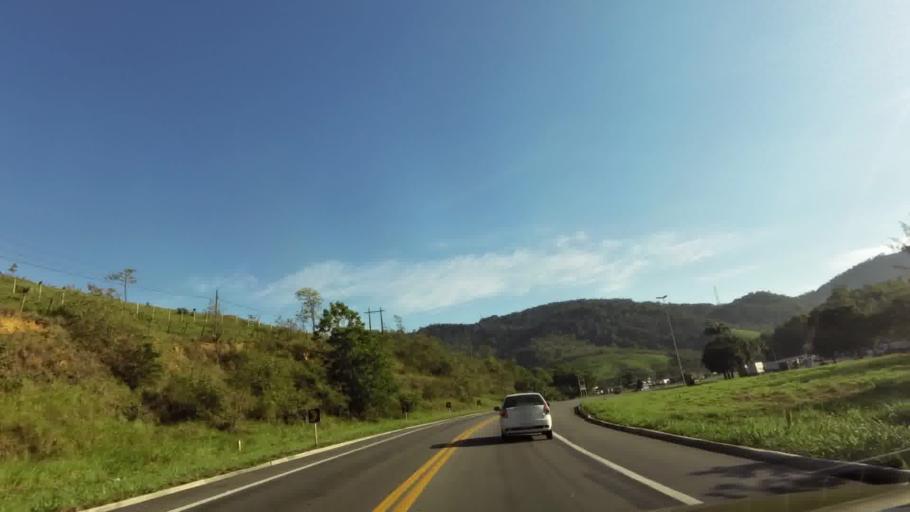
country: BR
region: Espirito Santo
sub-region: Viana
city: Viana
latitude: -20.3897
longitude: -40.4639
